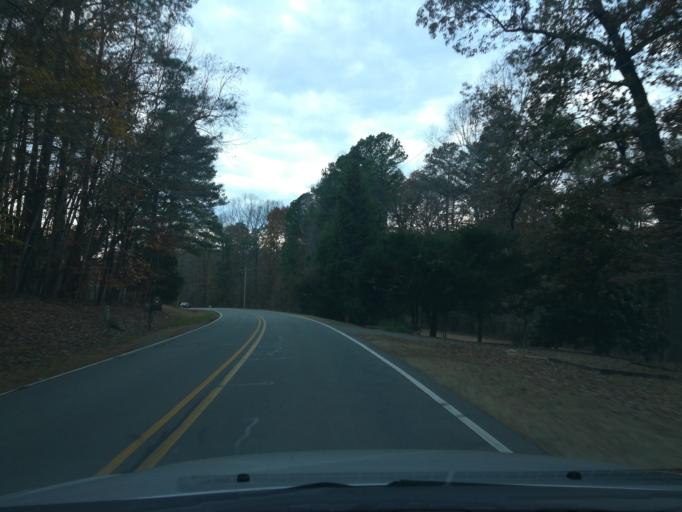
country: US
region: North Carolina
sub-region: Orange County
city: Chapel Hill
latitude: 35.9997
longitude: -79.0509
